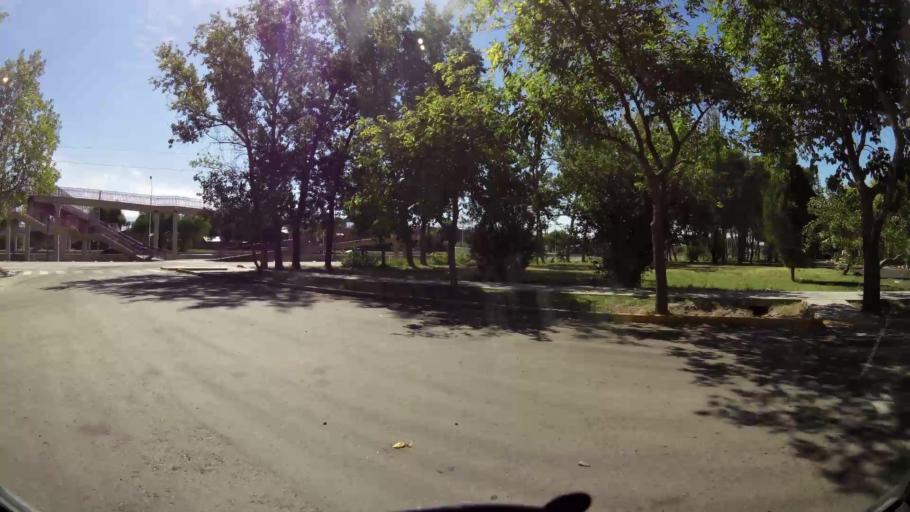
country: AR
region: Mendoza
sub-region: Departamento de Godoy Cruz
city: Godoy Cruz
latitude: -32.9567
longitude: -68.8353
